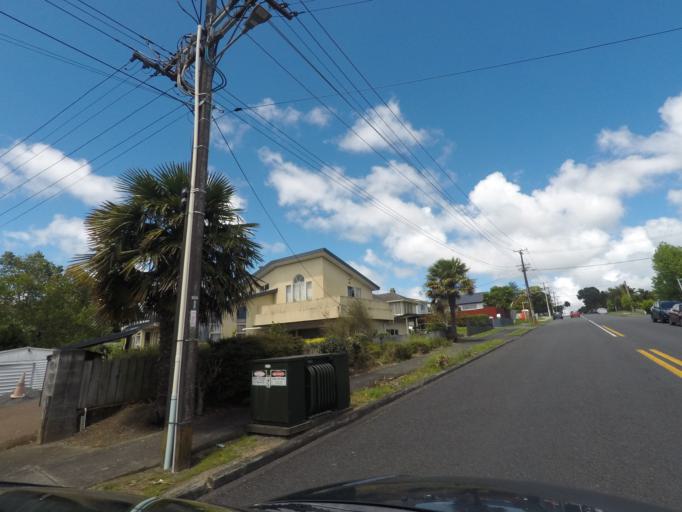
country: NZ
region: Auckland
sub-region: Auckland
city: Rosebank
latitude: -36.8771
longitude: 174.6430
